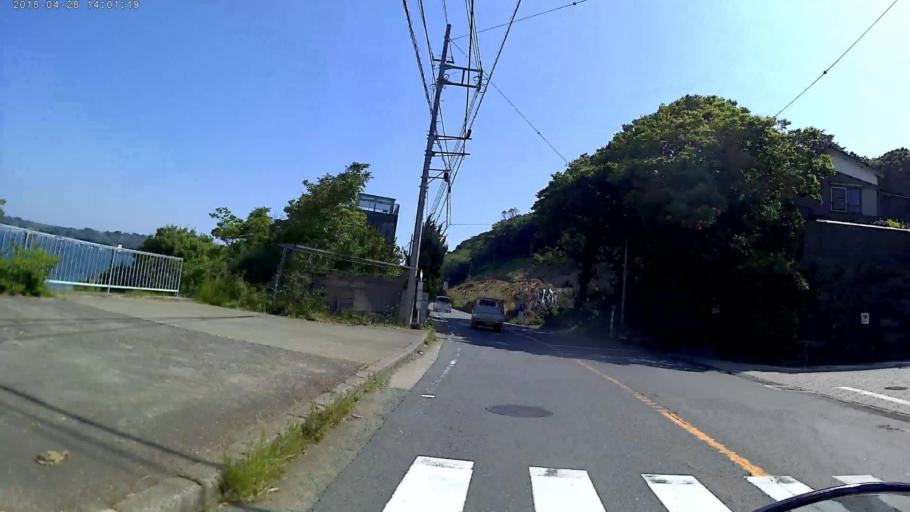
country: JP
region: Kanagawa
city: Miura
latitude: 35.1690
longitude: 139.6594
